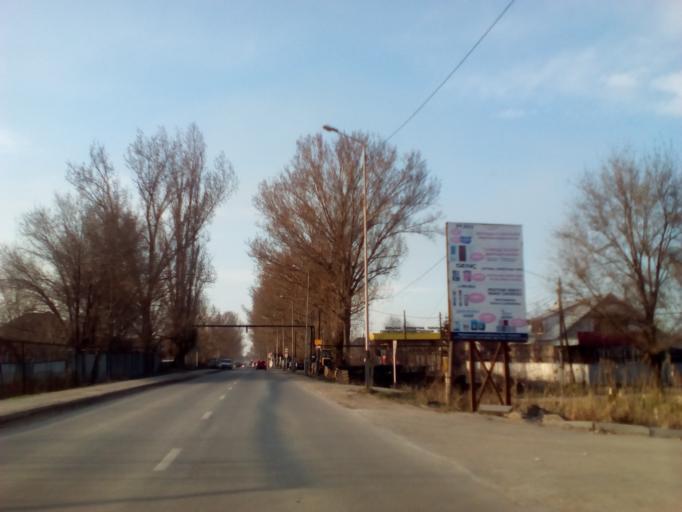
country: KZ
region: Almaty Oblysy
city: Burunday
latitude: 43.2526
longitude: 76.7832
